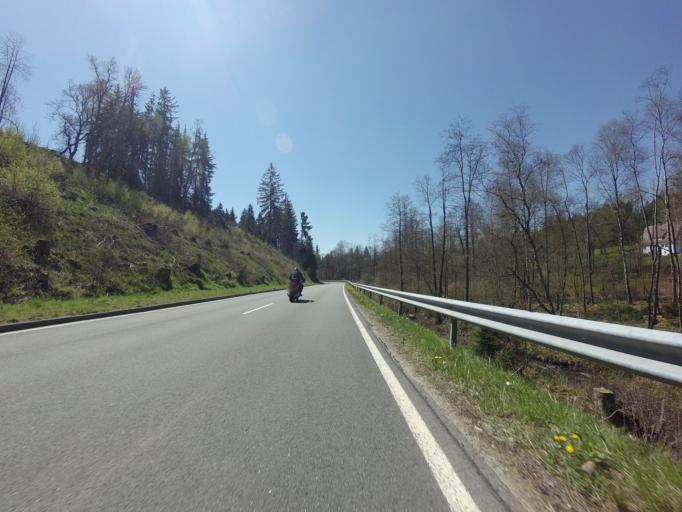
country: DE
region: North Rhine-Westphalia
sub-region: Regierungsbezirk Arnsberg
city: Erndtebruck
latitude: 51.0565
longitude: 8.2302
